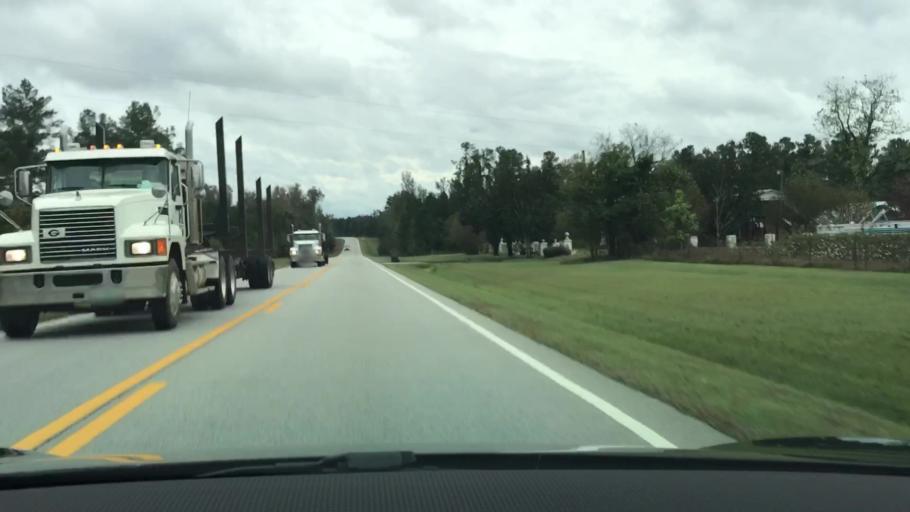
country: US
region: Georgia
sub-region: Glascock County
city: Gibson
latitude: 33.2706
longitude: -82.4963
